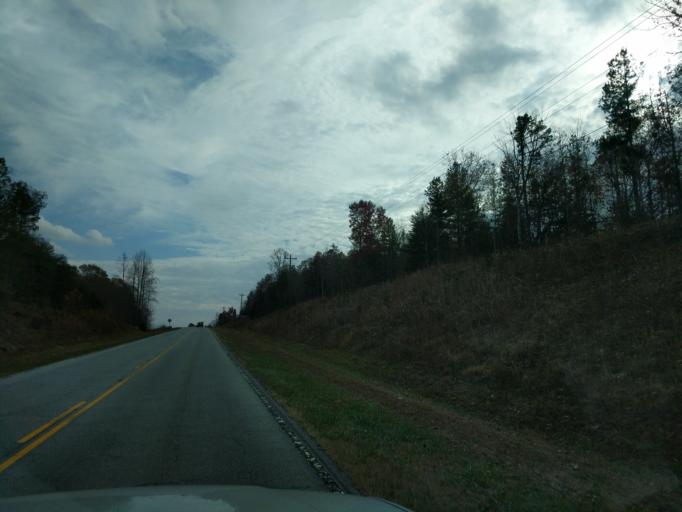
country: US
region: Georgia
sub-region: Franklin County
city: Gumlog
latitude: 34.5303
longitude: -83.0530
